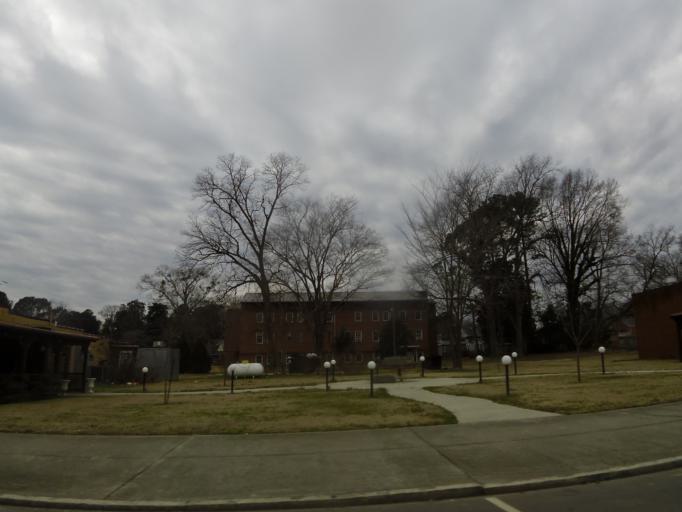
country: US
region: North Carolina
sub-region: Halifax County
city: Scotland Neck
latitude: 36.1287
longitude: -77.4241
